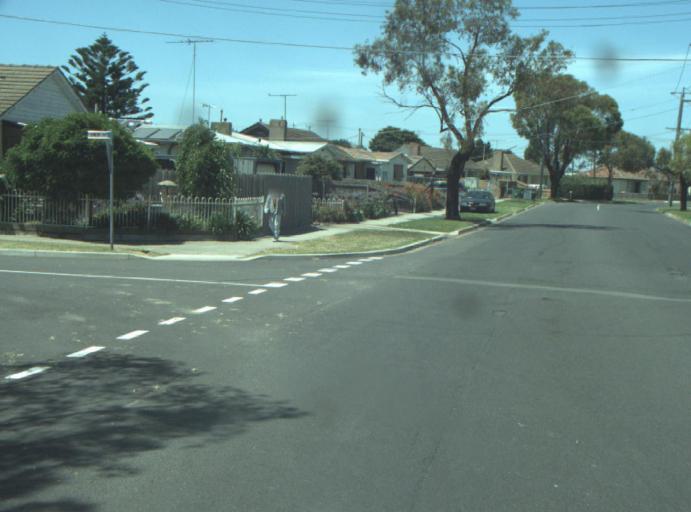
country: AU
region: Victoria
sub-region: Greater Geelong
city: Bell Park
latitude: -38.0891
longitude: 144.3542
